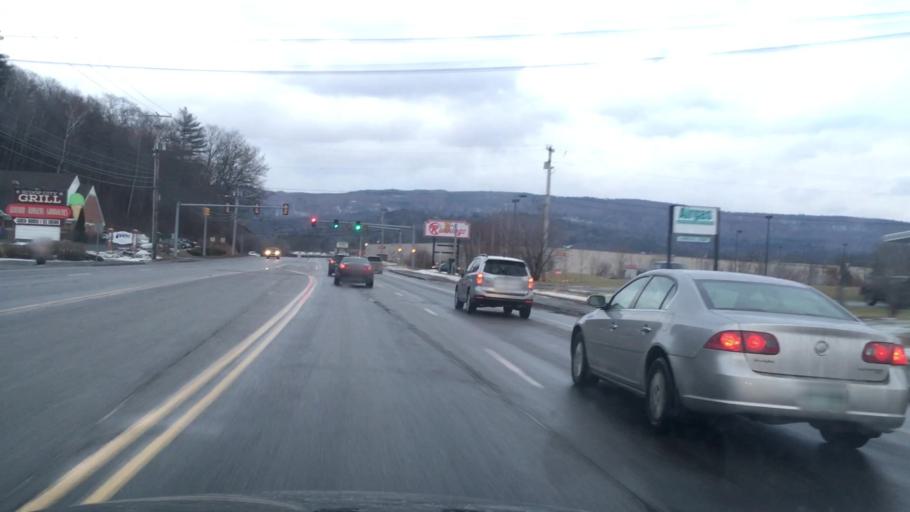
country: US
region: New Hampshire
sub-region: Sullivan County
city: Claremont
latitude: 43.3629
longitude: -72.3155
